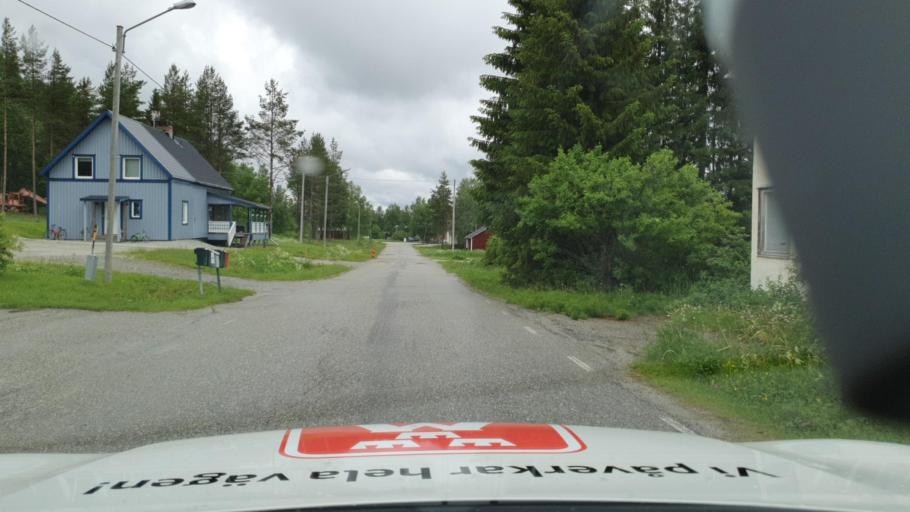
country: SE
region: Vaesterbotten
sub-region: Dorotea Kommun
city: Dorotea
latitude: 64.1002
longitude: 16.6449
